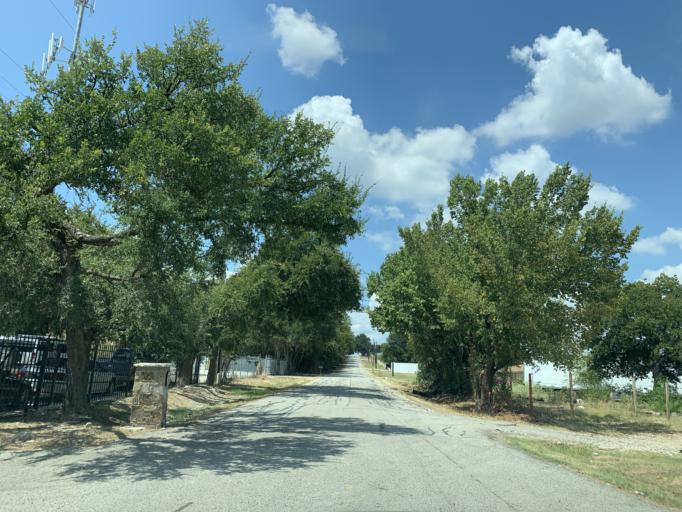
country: US
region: Texas
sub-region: Tarrant County
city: Lakeside
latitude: 32.8417
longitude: -97.4968
